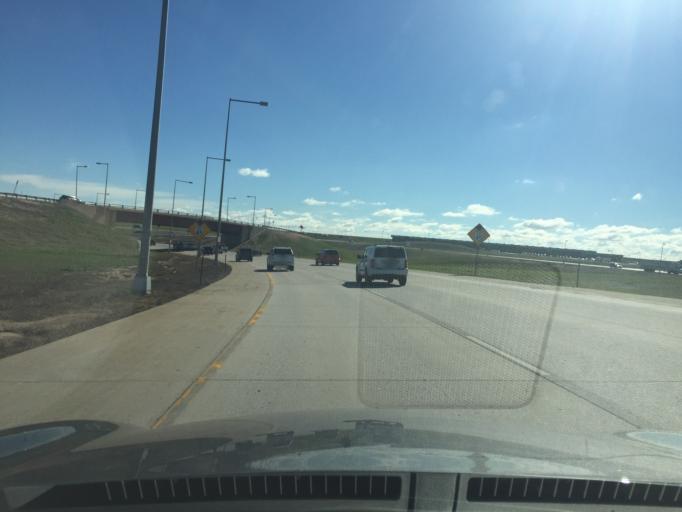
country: US
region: Colorado
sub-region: Weld County
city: Lochbuie
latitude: 39.8336
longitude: -104.6744
